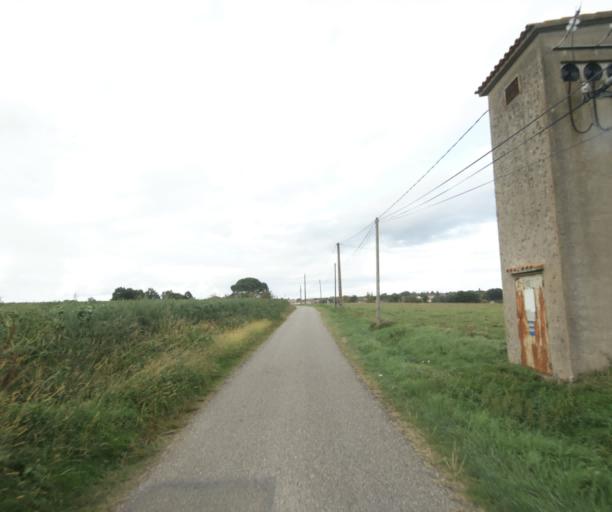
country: FR
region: Midi-Pyrenees
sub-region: Departement du Gers
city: Eauze
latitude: 43.9413
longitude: 0.0818
